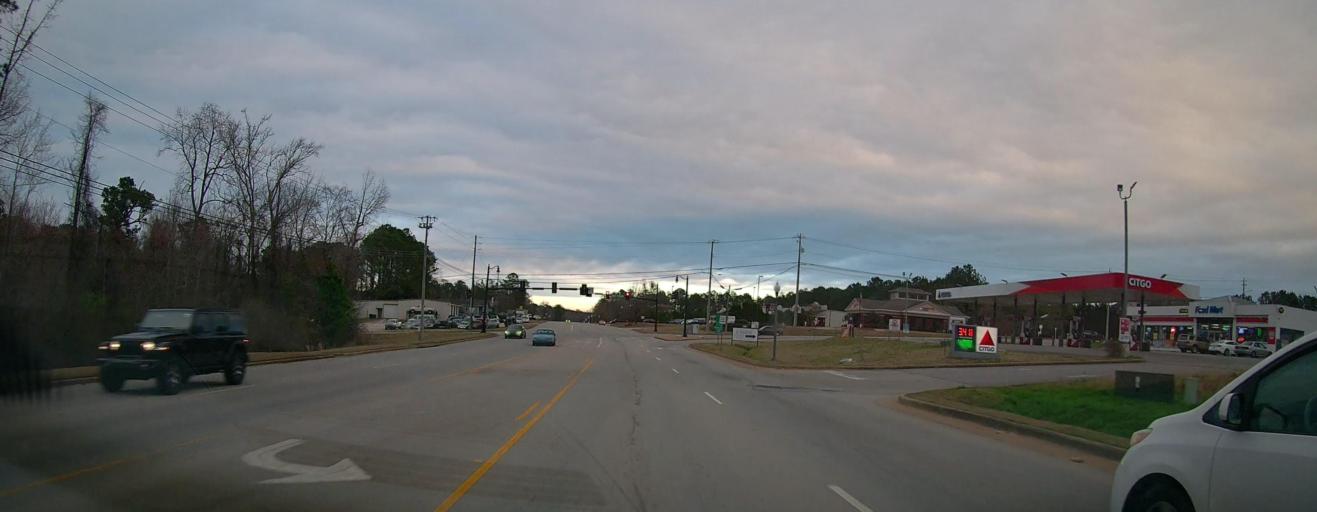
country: US
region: Alabama
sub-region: Chambers County
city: Valley
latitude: 32.8175
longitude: -85.1996
